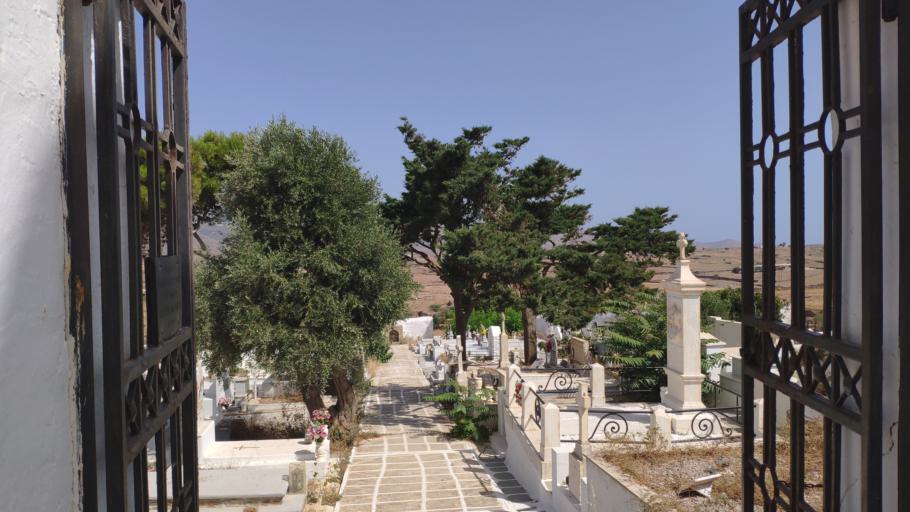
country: GR
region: South Aegean
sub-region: Nomos Kykladon
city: Kythnos
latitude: 37.4134
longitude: 24.4295
